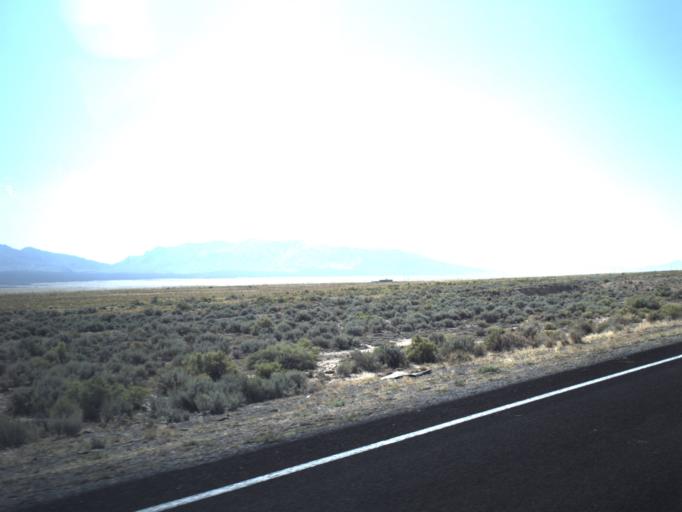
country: US
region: Utah
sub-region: Beaver County
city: Milford
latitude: 38.4763
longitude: -112.9915
